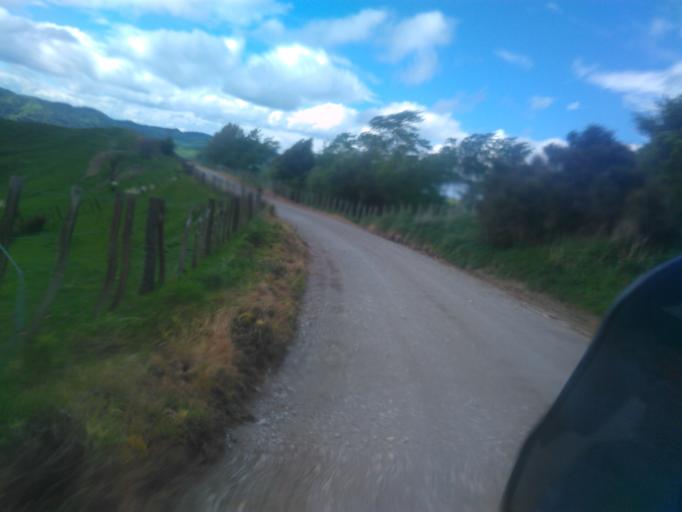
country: NZ
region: Hawke's Bay
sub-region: Wairoa District
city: Wairoa
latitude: -38.7676
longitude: 177.6401
